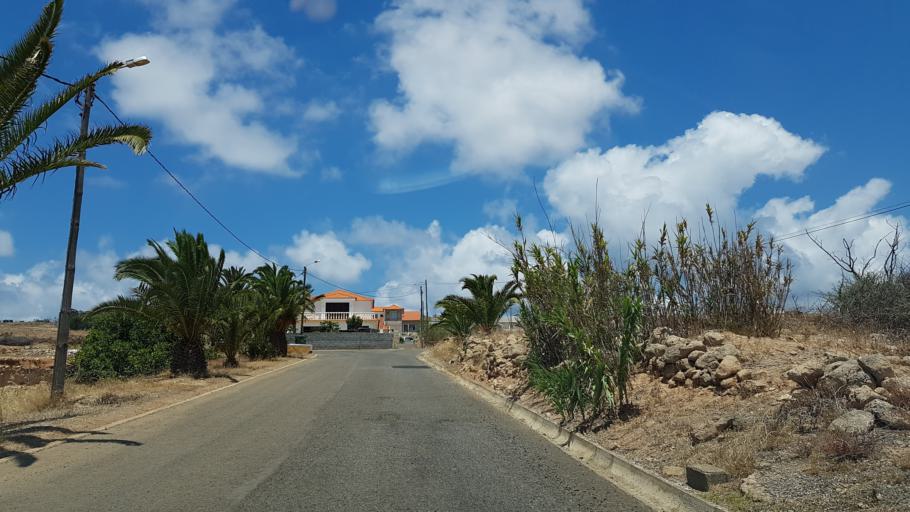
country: PT
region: Madeira
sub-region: Porto Santo
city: Vila de Porto Santo
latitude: 33.0625
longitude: -16.3608
